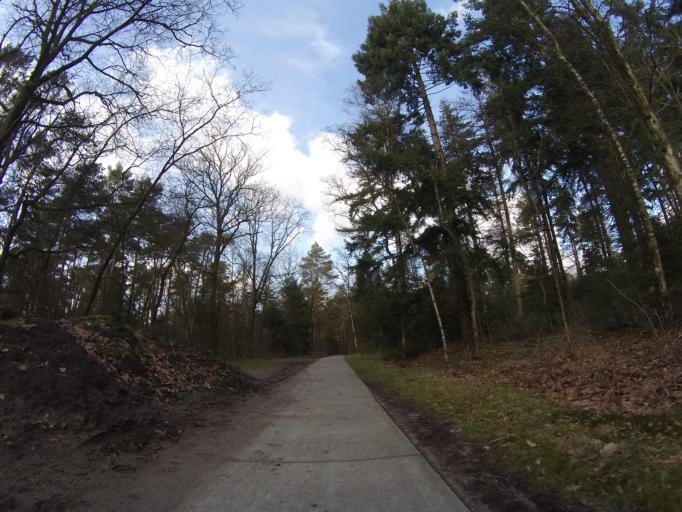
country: NL
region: Utrecht
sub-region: Gemeente Soest
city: Soest
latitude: 52.1485
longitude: 5.2552
